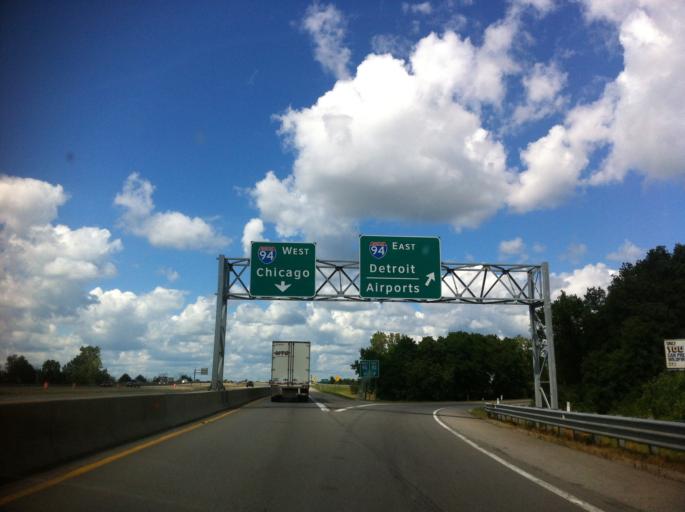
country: US
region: Michigan
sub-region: Washtenaw County
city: Ypsilanti
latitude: 42.2199
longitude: -83.6851
